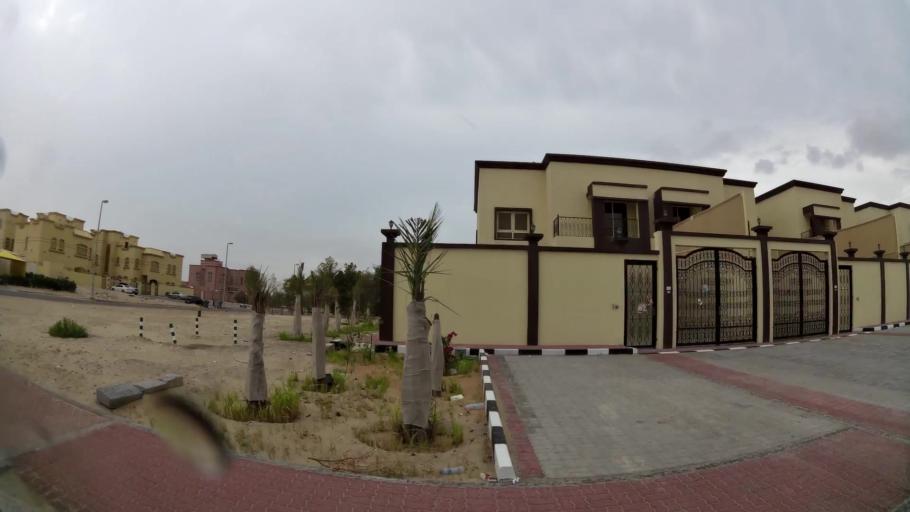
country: AE
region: Abu Dhabi
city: Abu Dhabi
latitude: 24.3662
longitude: 54.6457
